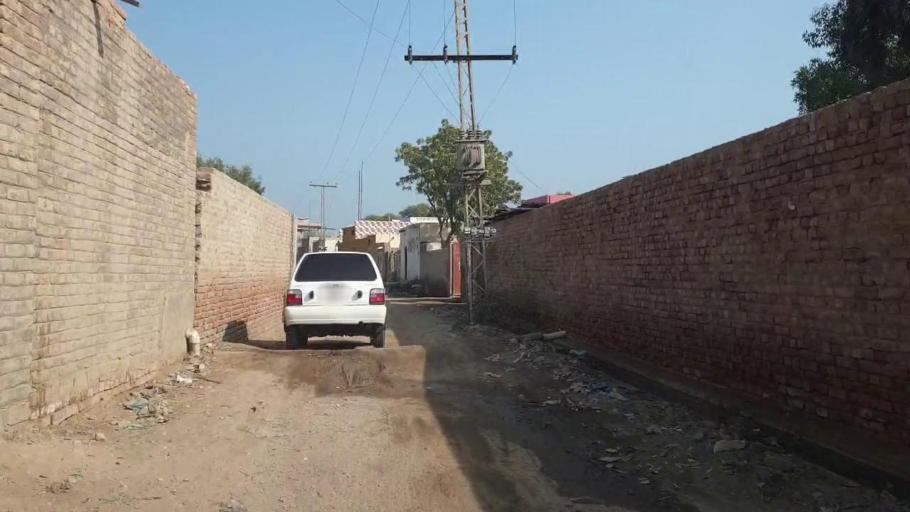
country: PK
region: Sindh
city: Bhit Shah
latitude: 25.7208
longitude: 68.5246
